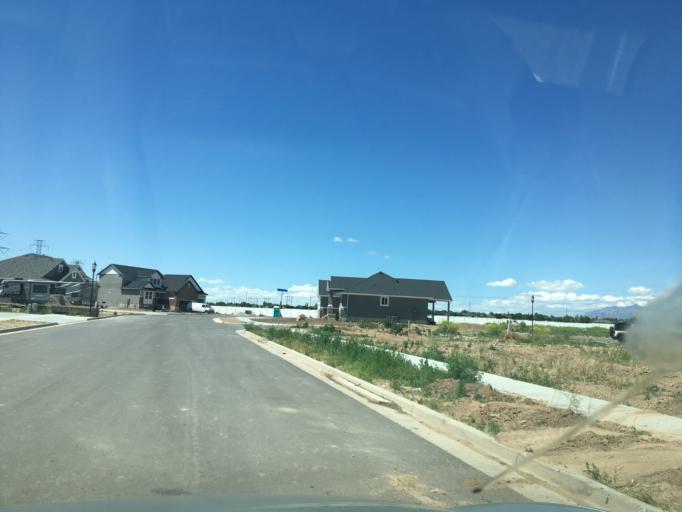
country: US
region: Utah
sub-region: Davis County
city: Layton
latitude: 41.0615
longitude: -112.0106
